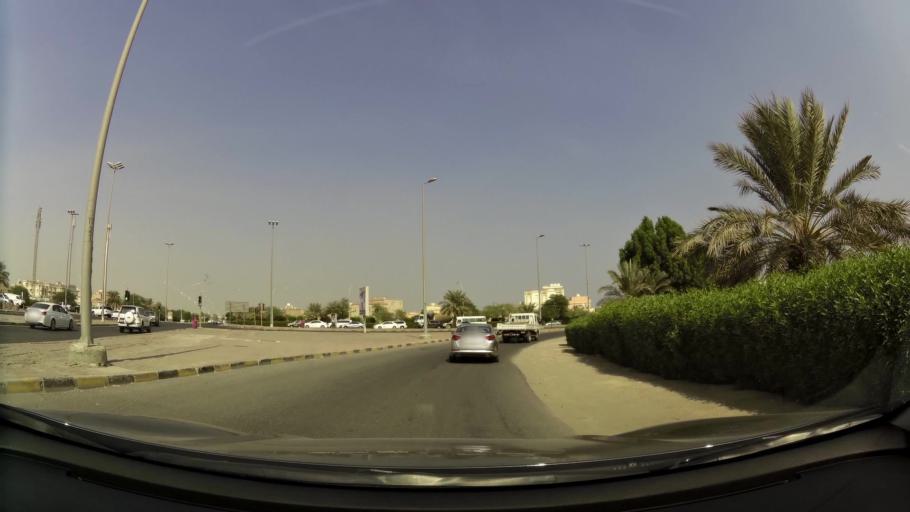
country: KW
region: Al Ahmadi
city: Al Fahahil
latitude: 29.0916
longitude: 48.1061
